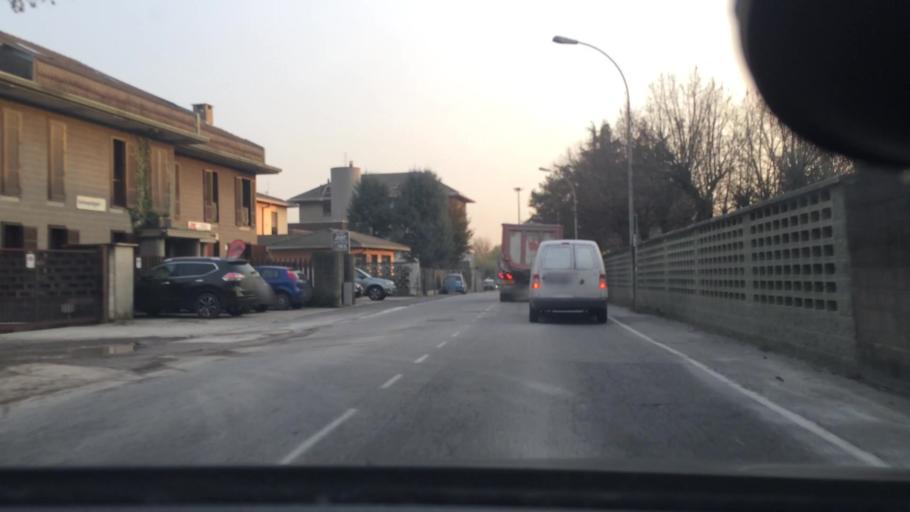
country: IT
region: Lombardy
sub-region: Provincia di Monza e Brianza
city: Villaggio del Sole
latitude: 45.6221
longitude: 9.1028
